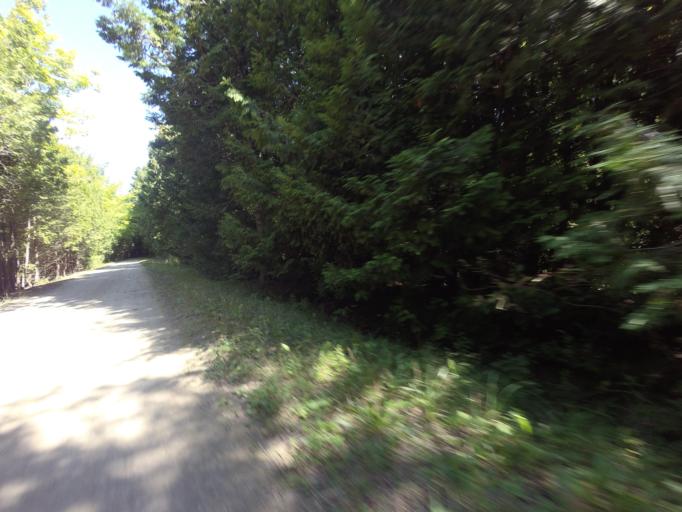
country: CA
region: Ontario
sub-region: Wellington County
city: Guelph
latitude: 43.7835
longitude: -80.3238
